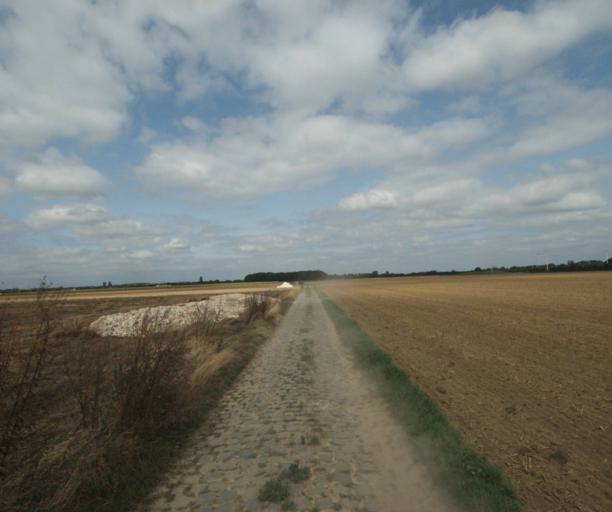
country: FR
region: Nord-Pas-de-Calais
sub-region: Departement du Nord
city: Baisieux
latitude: 50.5969
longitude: 3.2365
